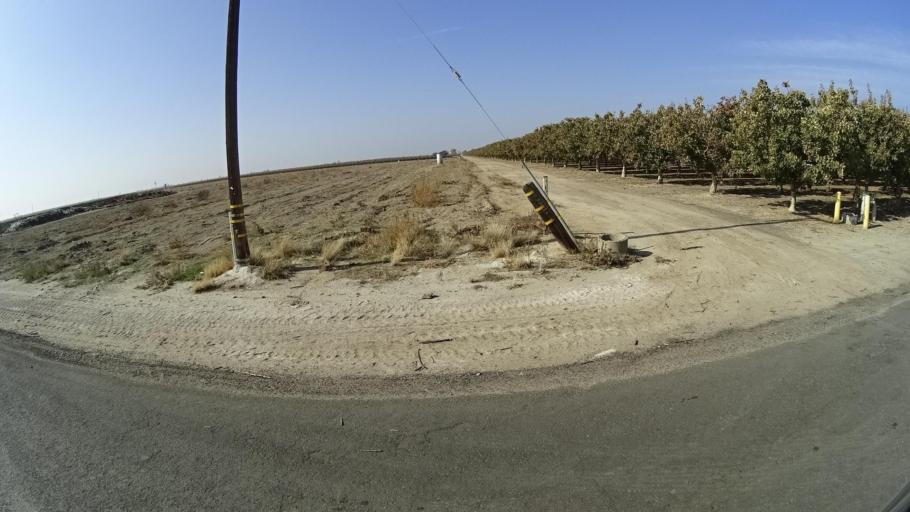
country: US
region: California
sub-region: Kern County
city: McFarland
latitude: 35.6527
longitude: -119.1868
